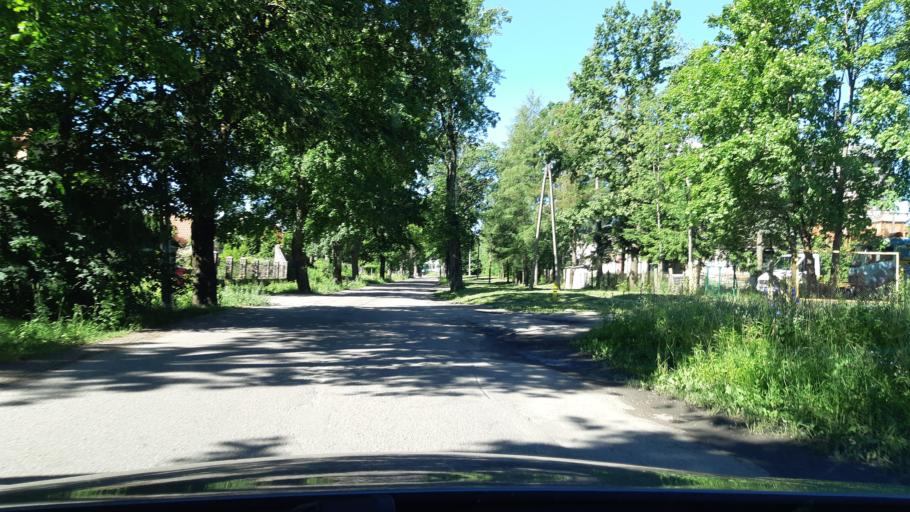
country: PL
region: Warmian-Masurian Voivodeship
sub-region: Powiat mragowski
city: Mragowo
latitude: 53.8552
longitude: 21.2960
